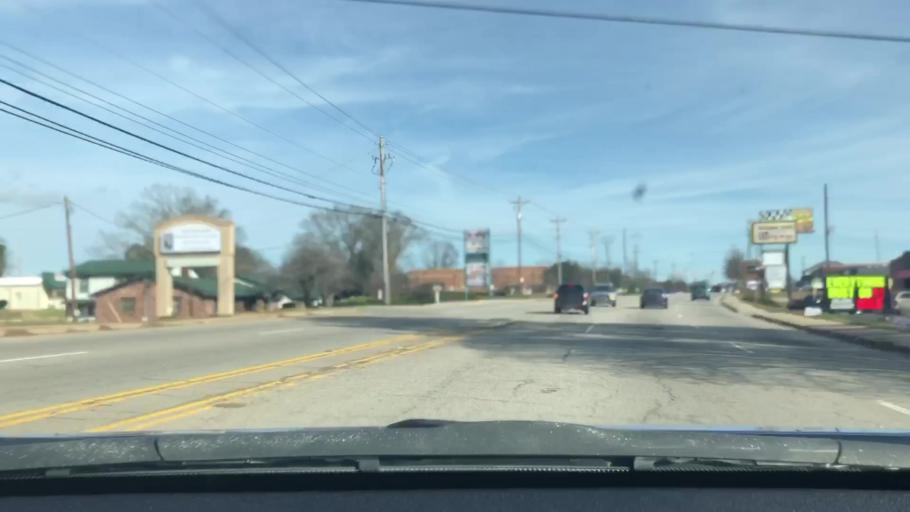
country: US
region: South Carolina
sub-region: Lexington County
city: Saint Andrews
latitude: 34.0493
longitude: -81.1089
